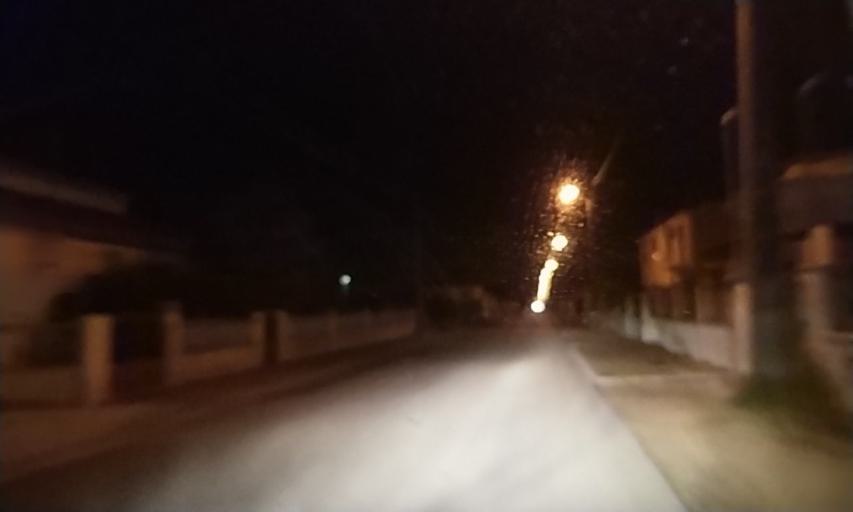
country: PT
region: Setubal
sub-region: Setubal
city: Setubal
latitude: 38.5214
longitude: -8.8008
